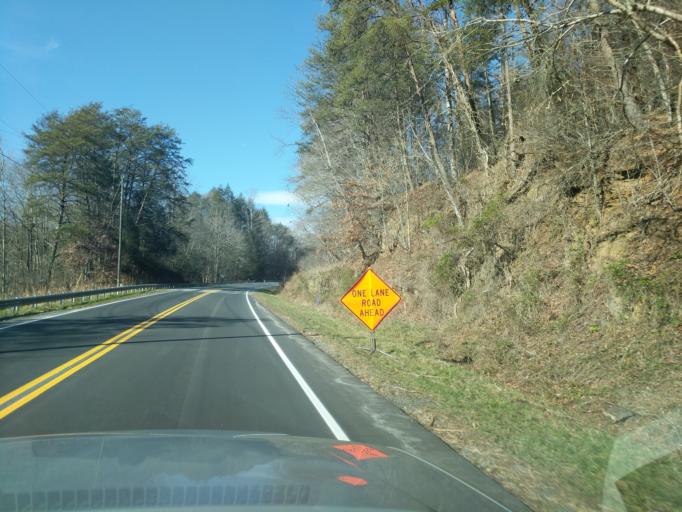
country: US
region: North Carolina
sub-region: McDowell County
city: West Marion
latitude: 35.5770
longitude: -81.9777
